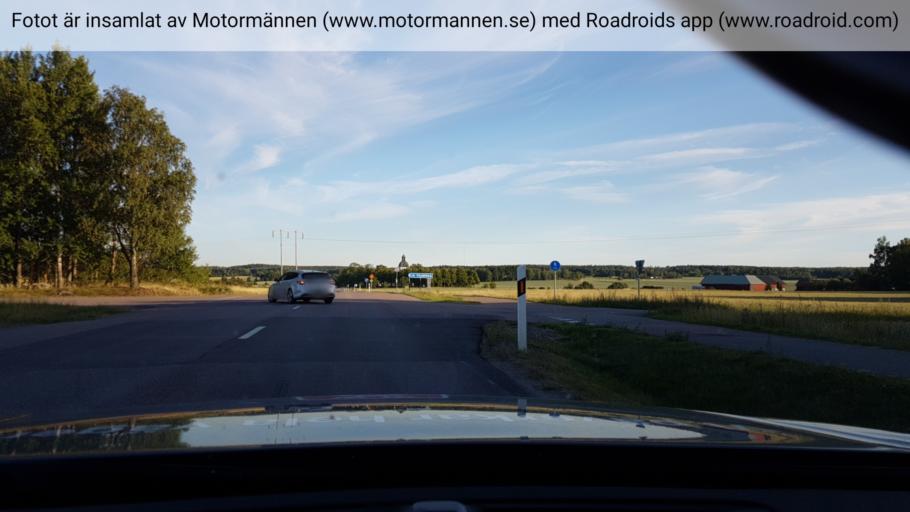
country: SE
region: Vaestmanland
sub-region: Vasteras
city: Skultuna
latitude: 59.7060
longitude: 16.4300
